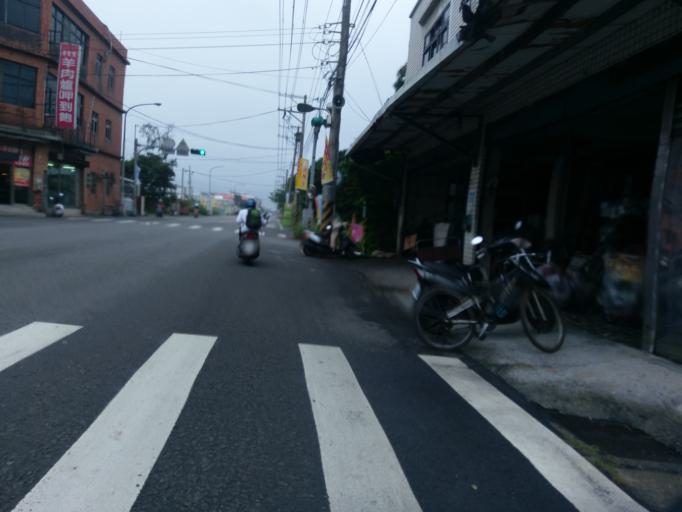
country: TW
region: Taiwan
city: Taoyuan City
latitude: 25.0654
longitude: 121.1922
